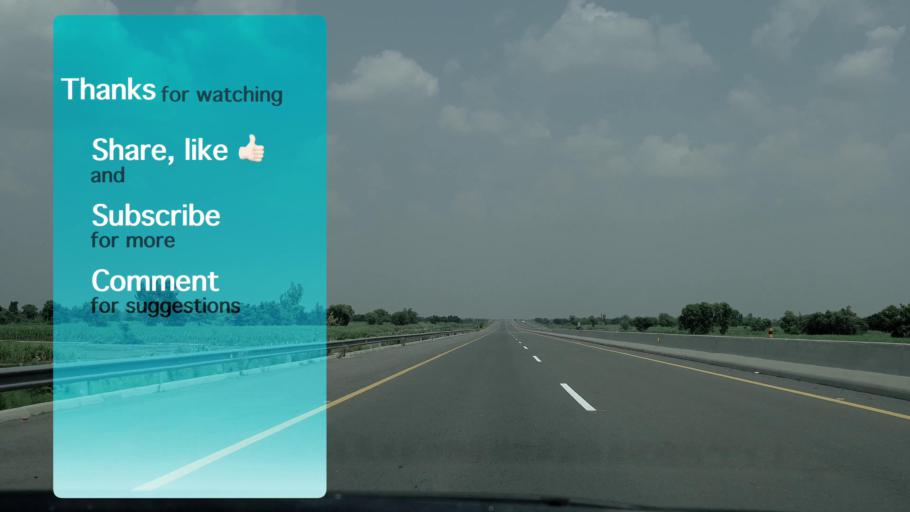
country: PK
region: Punjab
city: Gojra
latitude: 31.1983
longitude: 72.6568
